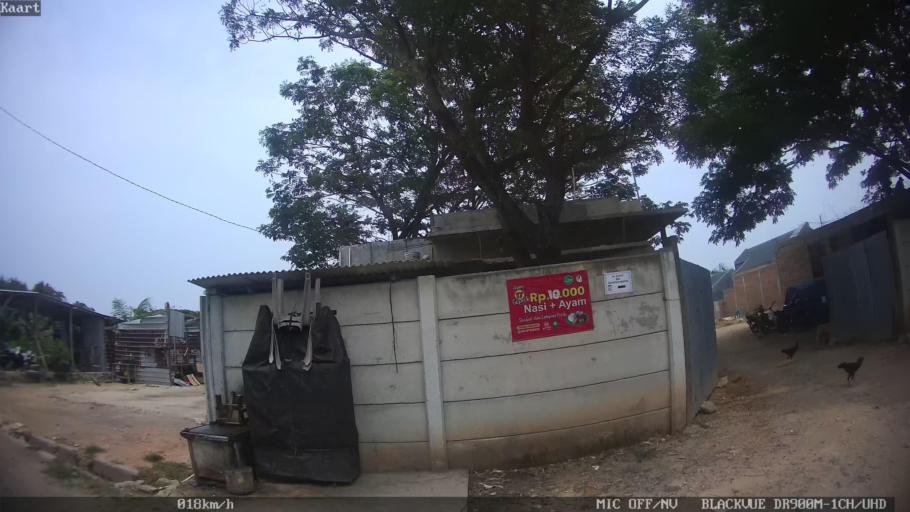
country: ID
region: Lampung
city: Kedaton
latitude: -5.4035
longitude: 105.3213
